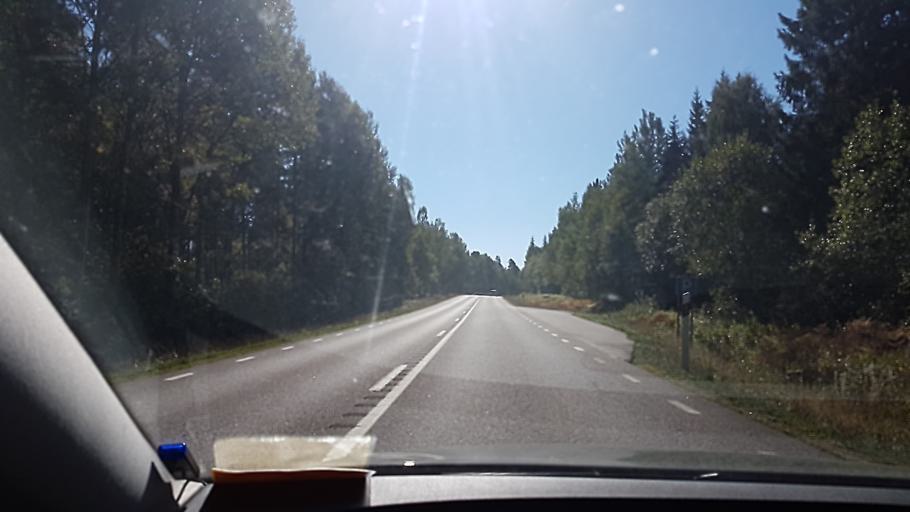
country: SE
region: Kronoberg
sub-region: Lessebo Kommun
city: Lessebo
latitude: 56.7728
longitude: 15.2578
